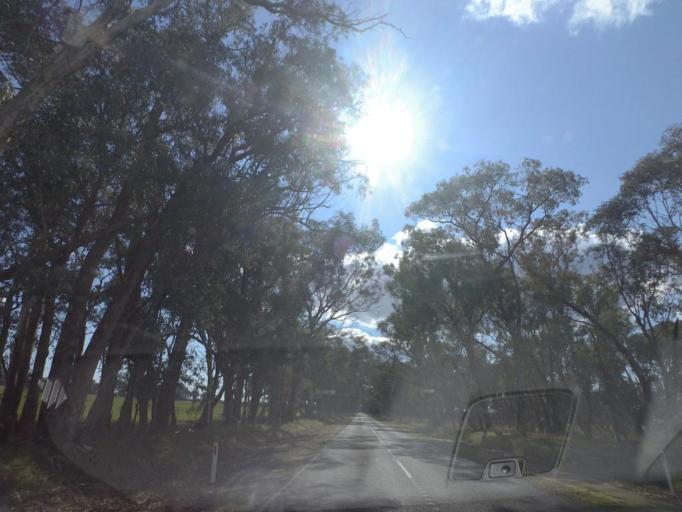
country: AU
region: New South Wales
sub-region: Corowa Shire
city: Howlong
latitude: -36.2251
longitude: 146.6288
